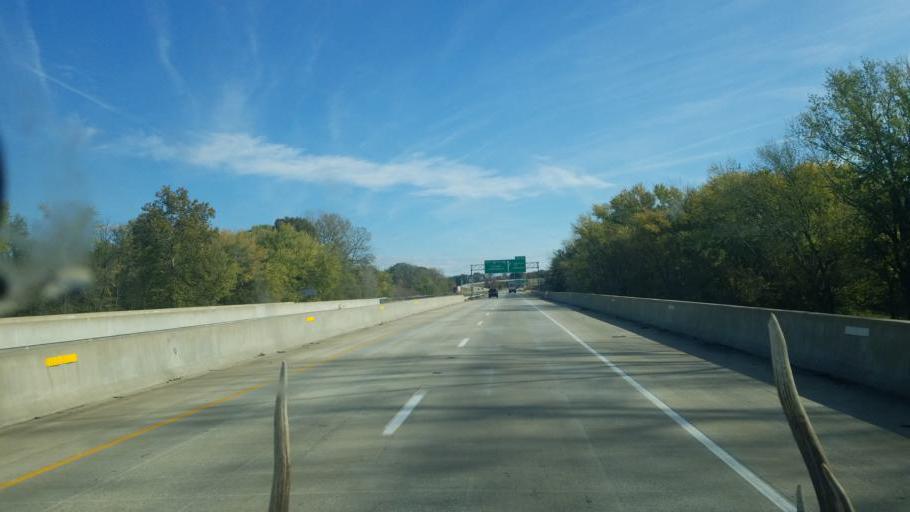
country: US
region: Illinois
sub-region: Effingham County
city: Effingham
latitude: 39.0902
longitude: -88.5951
